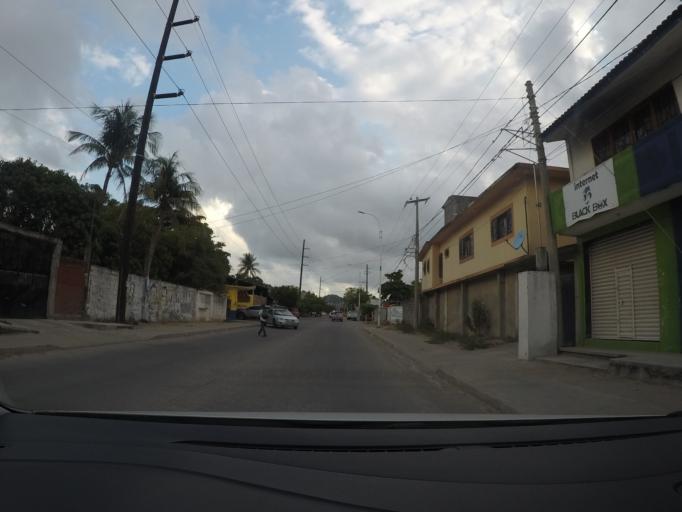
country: MX
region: Oaxaca
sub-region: Salina Cruz
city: Salina Cruz
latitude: 16.2055
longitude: -95.1974
